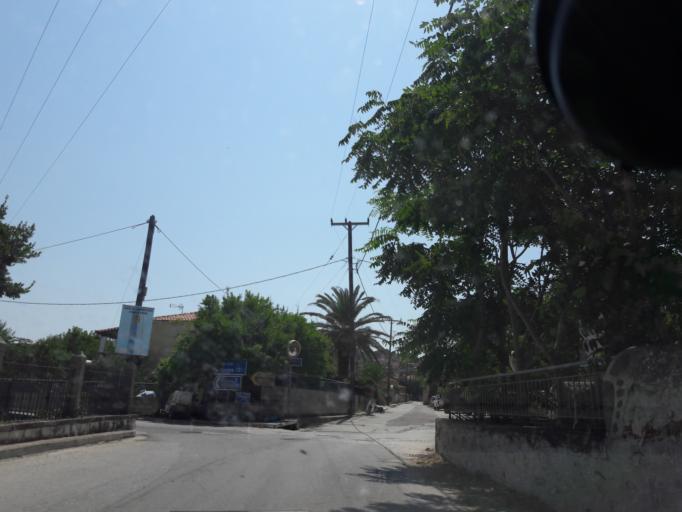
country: GR
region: North Aegean
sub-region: Nomos Lesvou
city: Myrina
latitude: 39.8667
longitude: 25.1517
